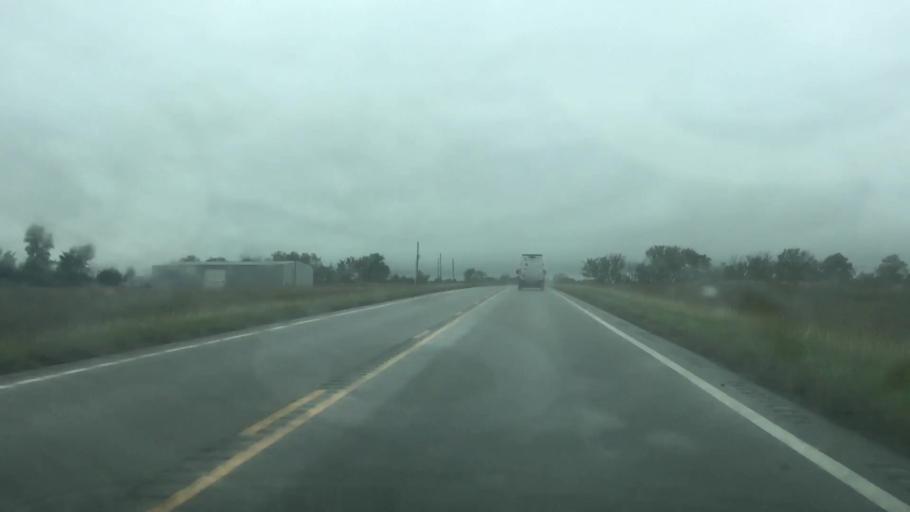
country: US
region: Kansas
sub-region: Anderson County
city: Garnett
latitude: 38.1570
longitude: -95.3122
